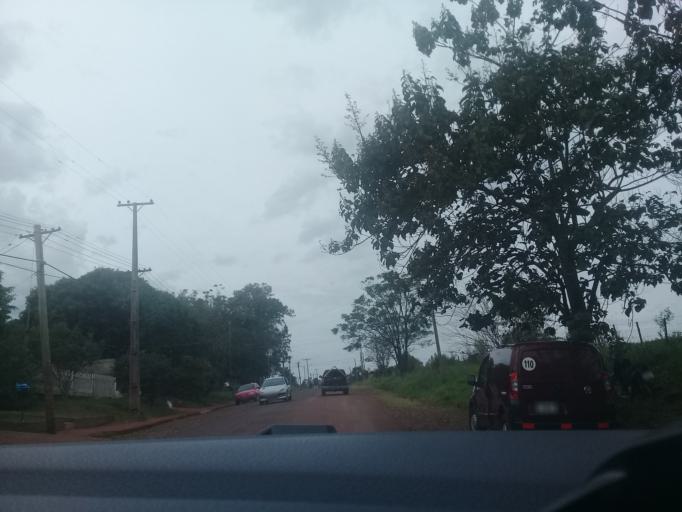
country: AR
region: Misiones
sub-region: Departamento de Obera
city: Obera
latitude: -27.4837
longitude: -55.1513
